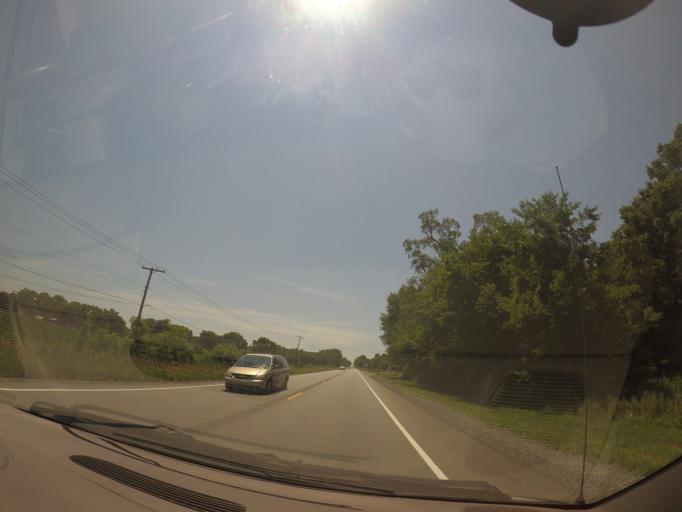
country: US
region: Indiana
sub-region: LaPorte County
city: Michigan City
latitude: 41.6354
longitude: -86.8945
